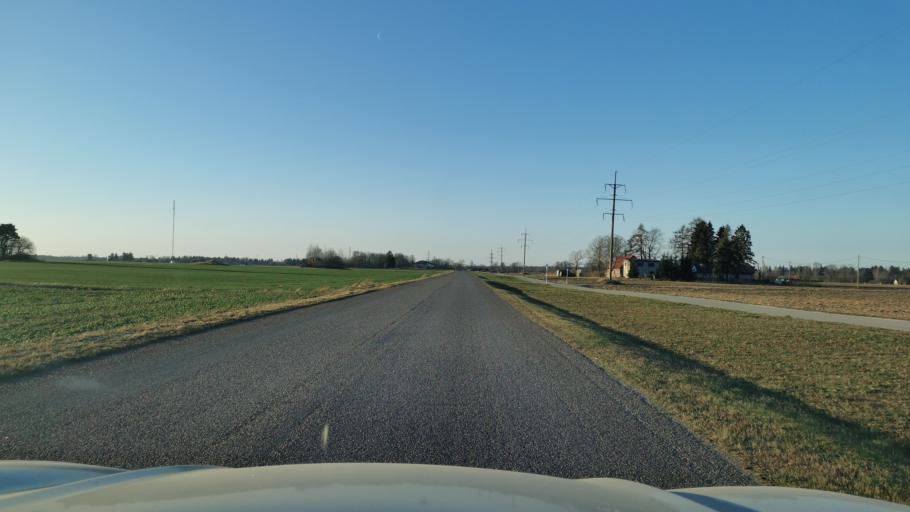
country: EE
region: Ida-Virumaa
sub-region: Puessi linn
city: Pussi
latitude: 59.3415
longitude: 27.0328
